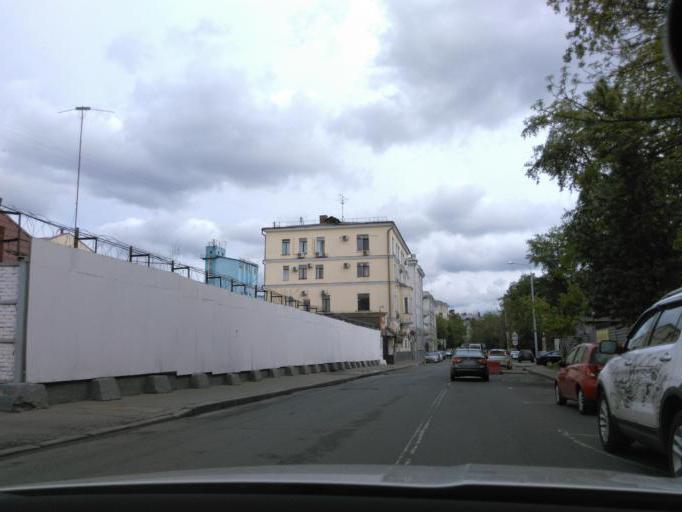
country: RU
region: Moscow
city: Zamoskvorech'ye
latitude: 55.7201
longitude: 37.6477
